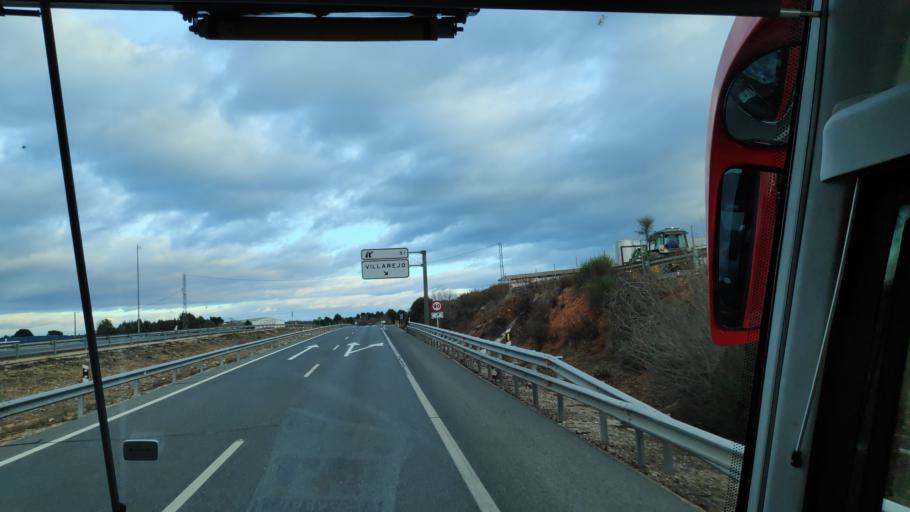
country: ES
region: Madrid
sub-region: Provincia de Madrid
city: Villarejo de Salvanes
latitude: 40.1637
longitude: -3.2739
